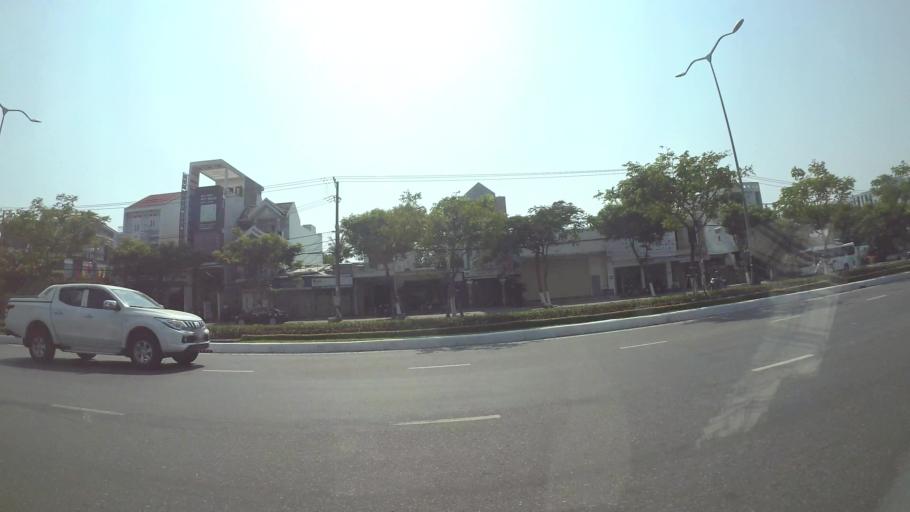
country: VN
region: Da Nang
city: Ngu Hanh Son
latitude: 16.0208
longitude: 108.2520
